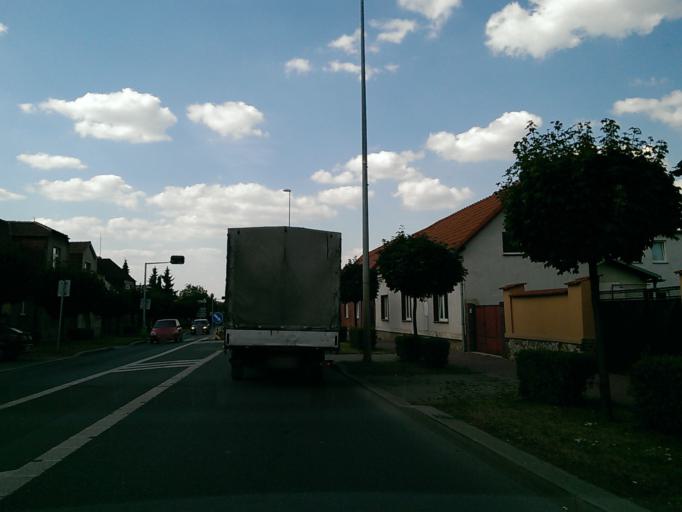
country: CZ
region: Praha
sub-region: Praha 14
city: Dolni Pocernice
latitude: 50.0597
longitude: 14.5584
